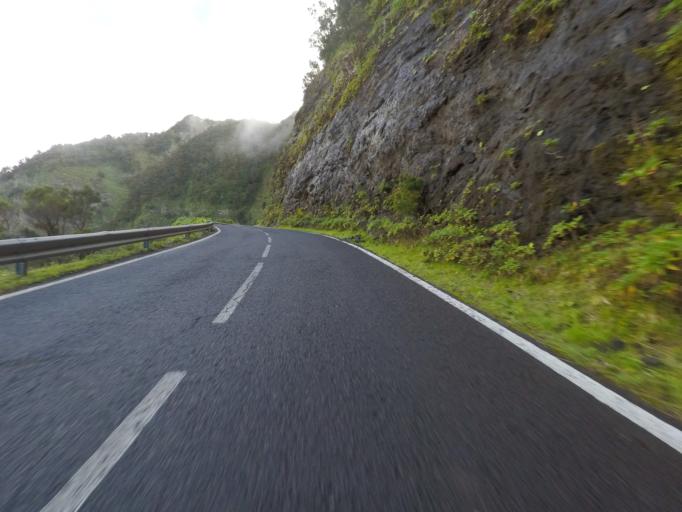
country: ES
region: Canary Islands
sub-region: Provincia de Santa Cruz de Tenerife
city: Hermigua
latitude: 28.1253
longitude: -17.2073
